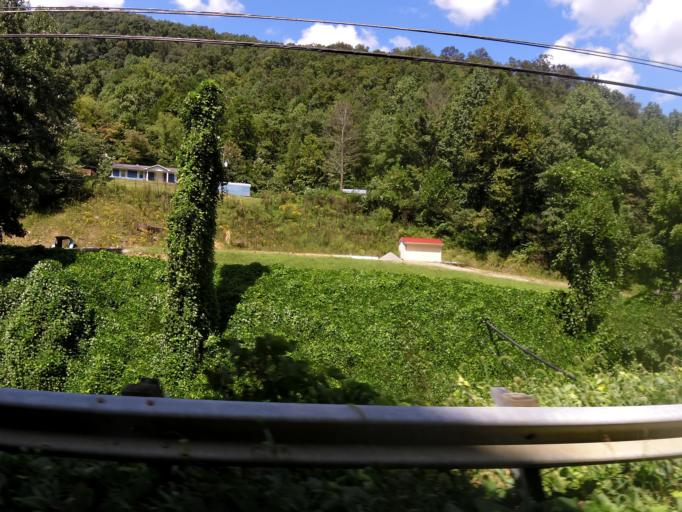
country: US
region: Kentucky
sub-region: Harlan County
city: Loyall
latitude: 36.9870
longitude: -83.3944
